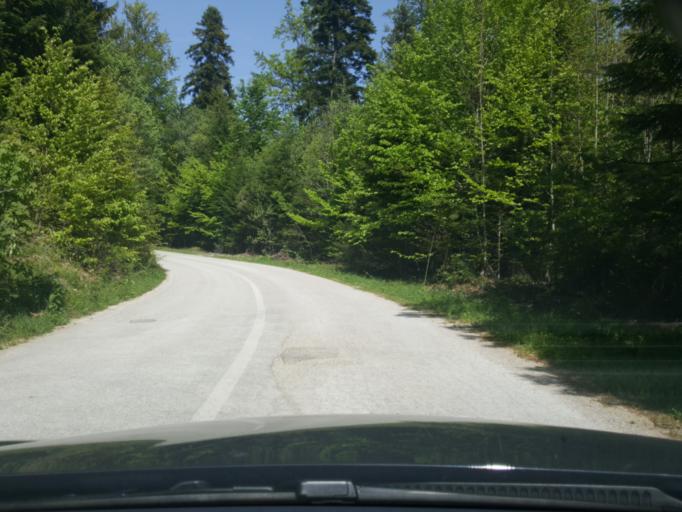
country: RS
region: Central Serbia
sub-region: Zlatiborski Okrug
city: Bajina Basta
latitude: 43.9100
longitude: 19.5012
